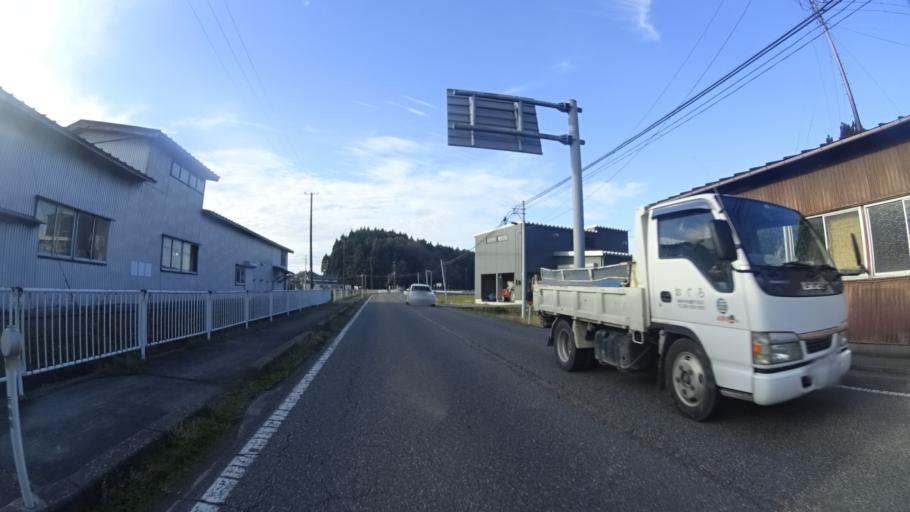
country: JP
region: Niigata
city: Yoshida-kasugacho
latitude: 37.6514
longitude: 138.8213
